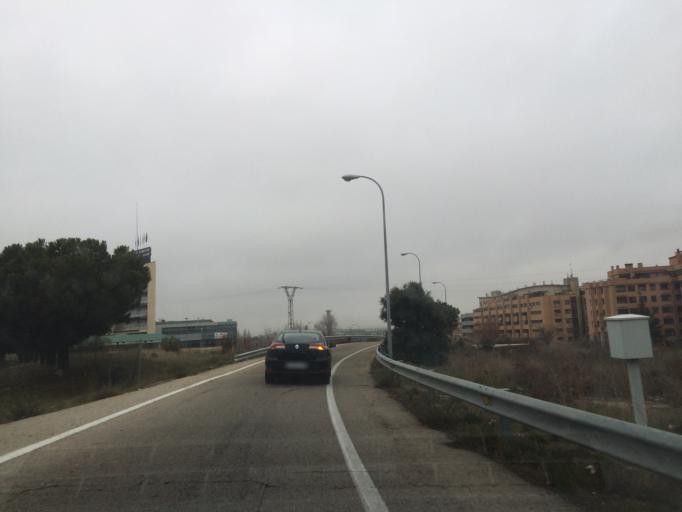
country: ES
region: Madrid
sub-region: Provincia de Madrid
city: Tres Cantos
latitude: 40.5956
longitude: -3.7144
